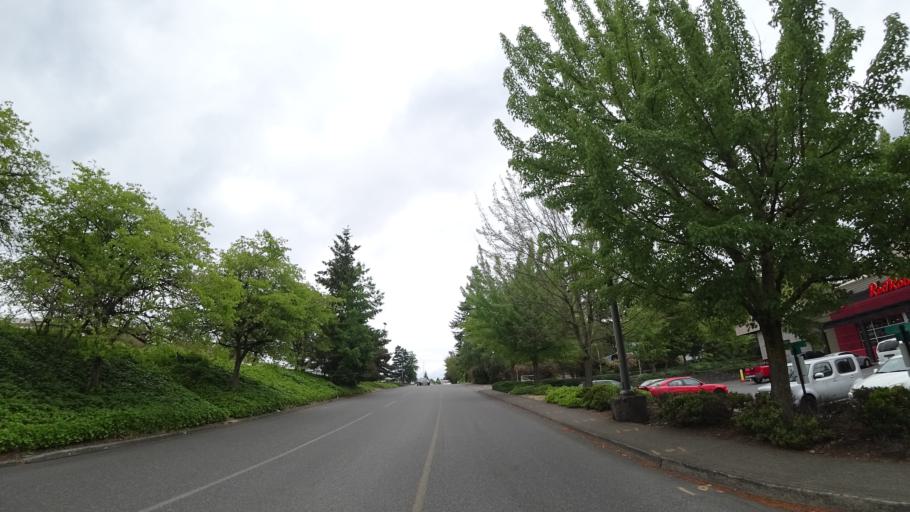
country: US
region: Oregon
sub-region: Washington County
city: Tigard
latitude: 45.4470
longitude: -122.7796
